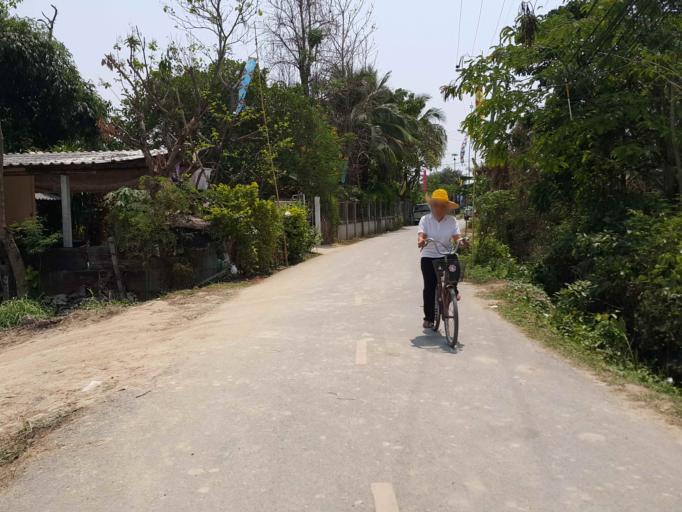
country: TH
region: Chiang Mai
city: San Kamphaeng
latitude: 18.7905
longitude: 99.0934
